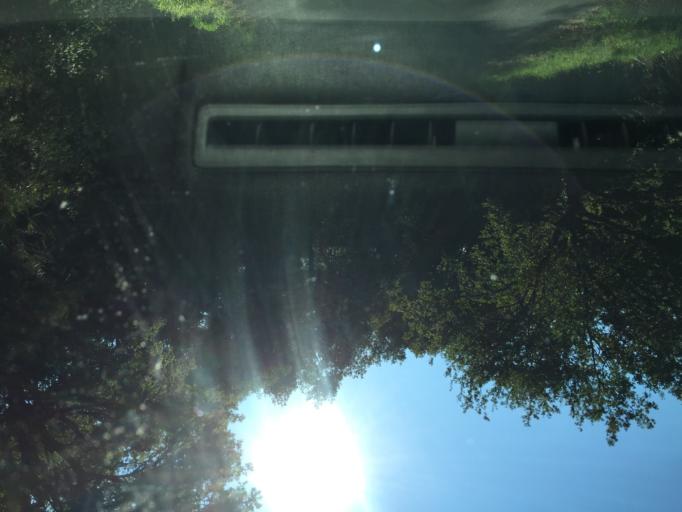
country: FR
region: Midi-Pyrenees
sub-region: Departement de l'Aveyron
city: Espalion
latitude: 44.5908
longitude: 2.6950
